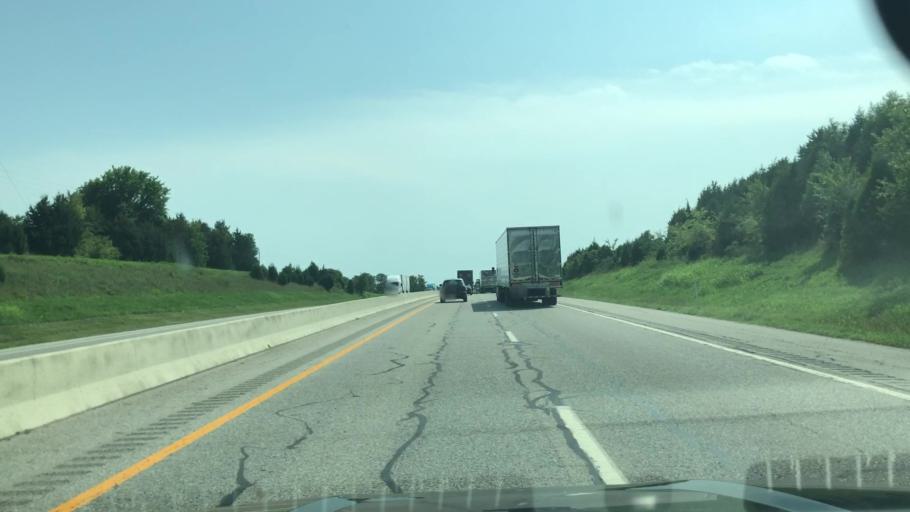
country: US
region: Oklahoma
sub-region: Ottawa County
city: Miami
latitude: 36.8349
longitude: -94.8644
